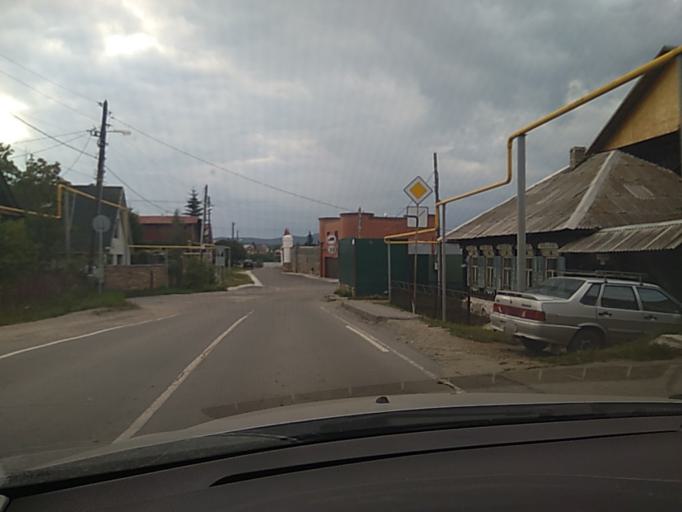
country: RU
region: Chelyabinsk
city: Kyshtym
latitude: 55.6999
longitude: 60.5319
